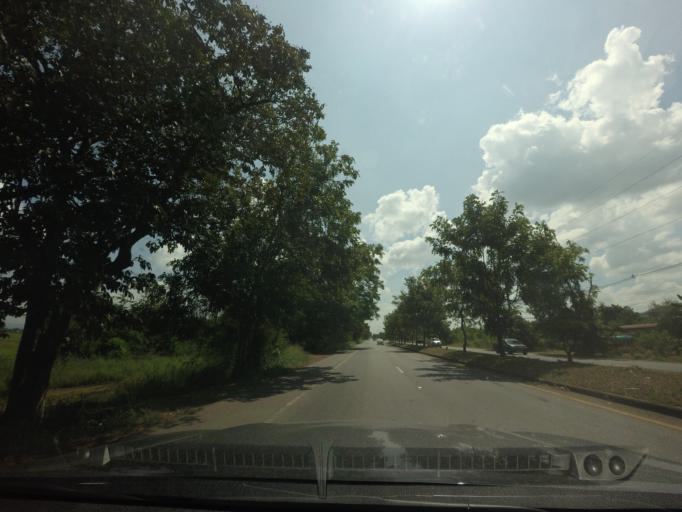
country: TH
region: Phetchabun
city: Nong Phai
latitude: 16.0419
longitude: 101.0798
